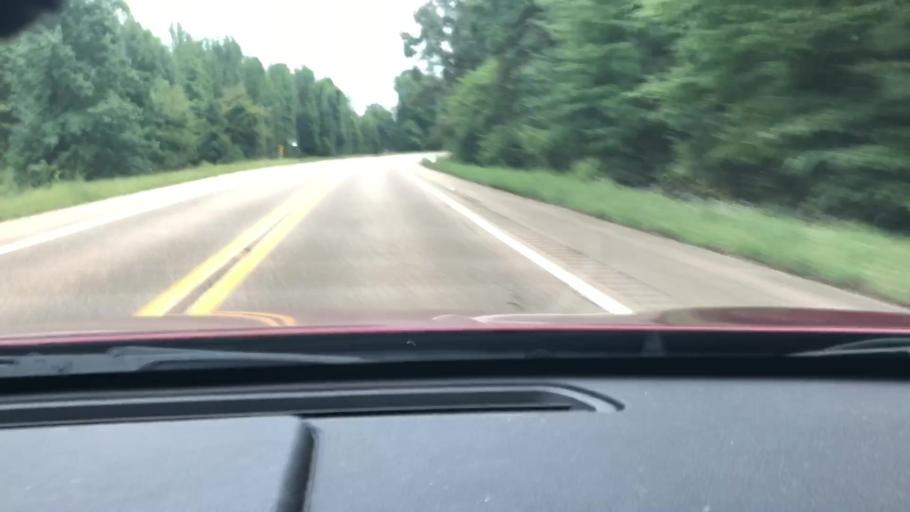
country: US
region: Arkansas
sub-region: Miller County
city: Texarkana
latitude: 33.4196
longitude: -93.8286
